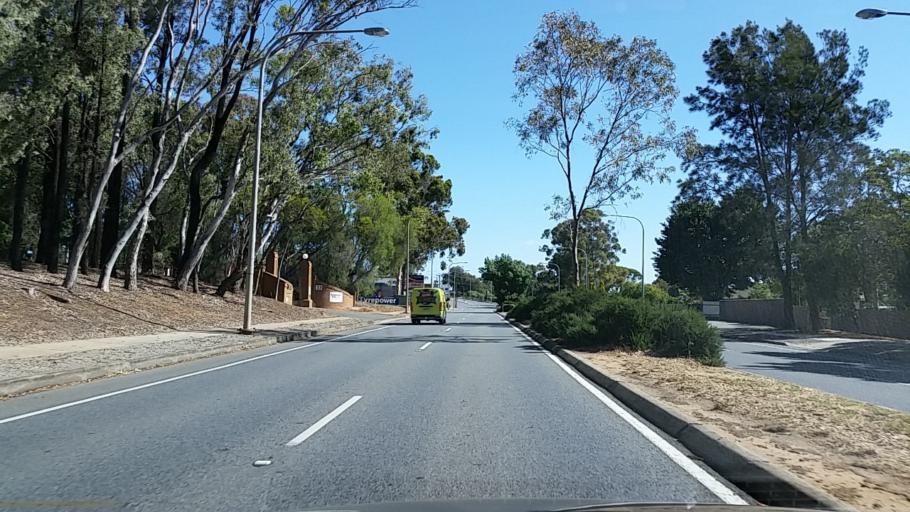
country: AU
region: South Australia
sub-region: Tea Tree Gully
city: Hope Valley
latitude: -34.8234
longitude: 138.6944
